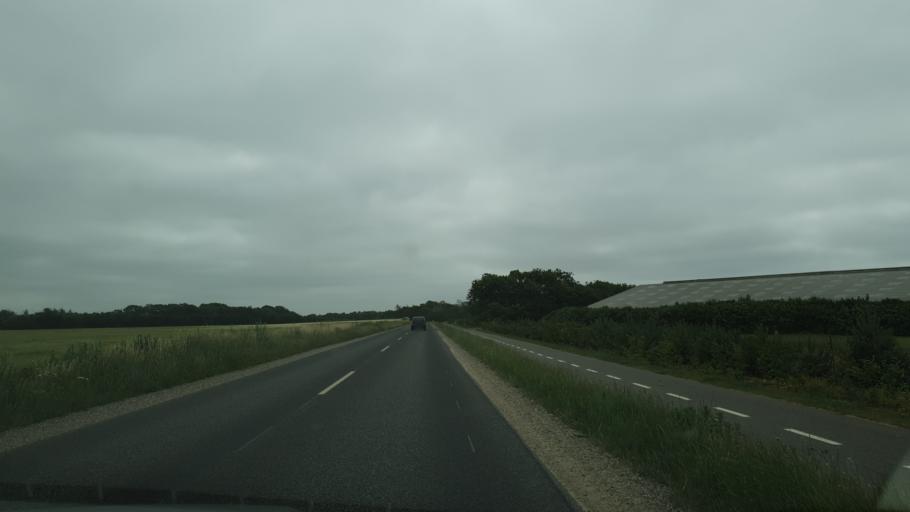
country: DK
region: Central Jutland
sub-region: Ringkobing-Skjern Kommune
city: Ringkobing
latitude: 55.9875
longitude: 8.3377
